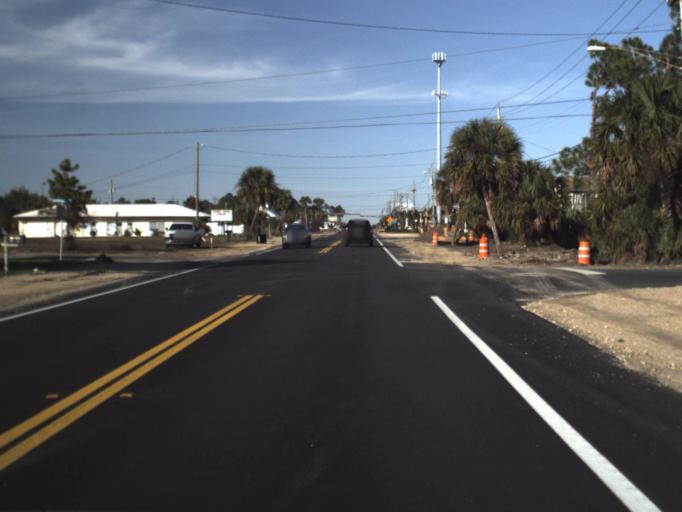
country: US
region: Florida
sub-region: Bay County
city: Laguna Beach
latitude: 30.2264
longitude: -85.8893
